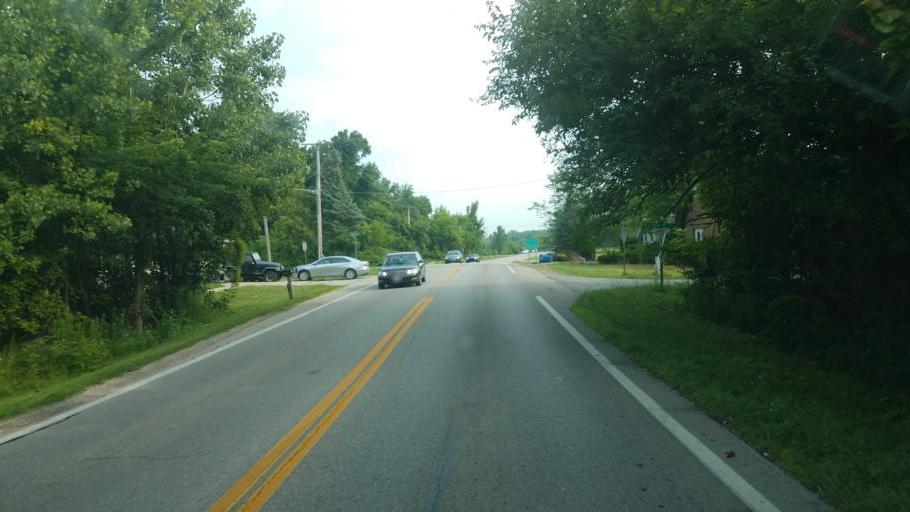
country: US
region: Ohio
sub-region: Delaware County
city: Powell
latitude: 40.1658
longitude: -83.1366
